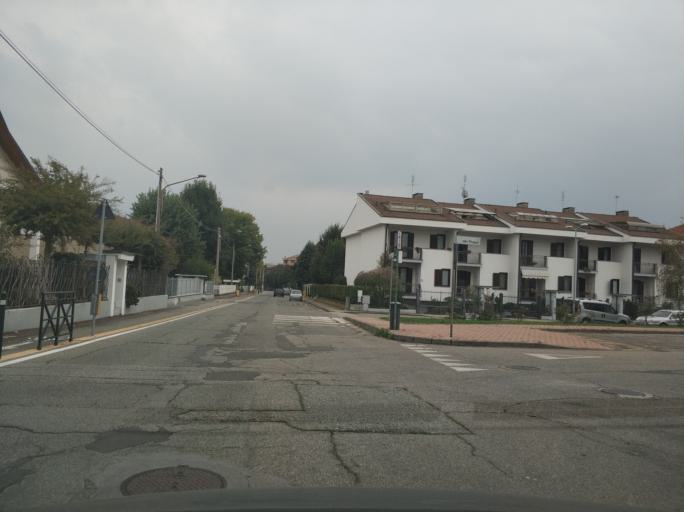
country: IT
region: Piedmont
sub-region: Provincia di Torino
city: Cirie
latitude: 45.2292
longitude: 7.5966
